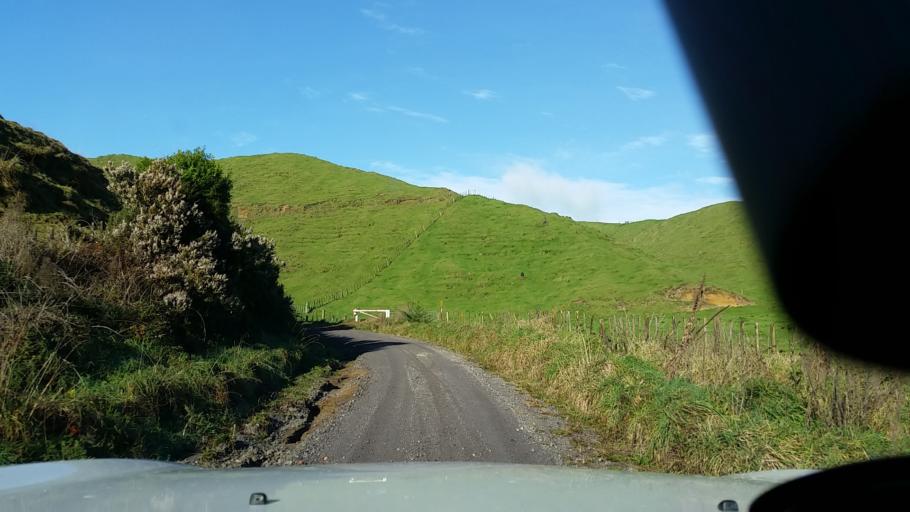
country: NZ
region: Bay of Plenty
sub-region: Kawerau District
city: Kawerau
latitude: -38.0102
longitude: 176.5658
